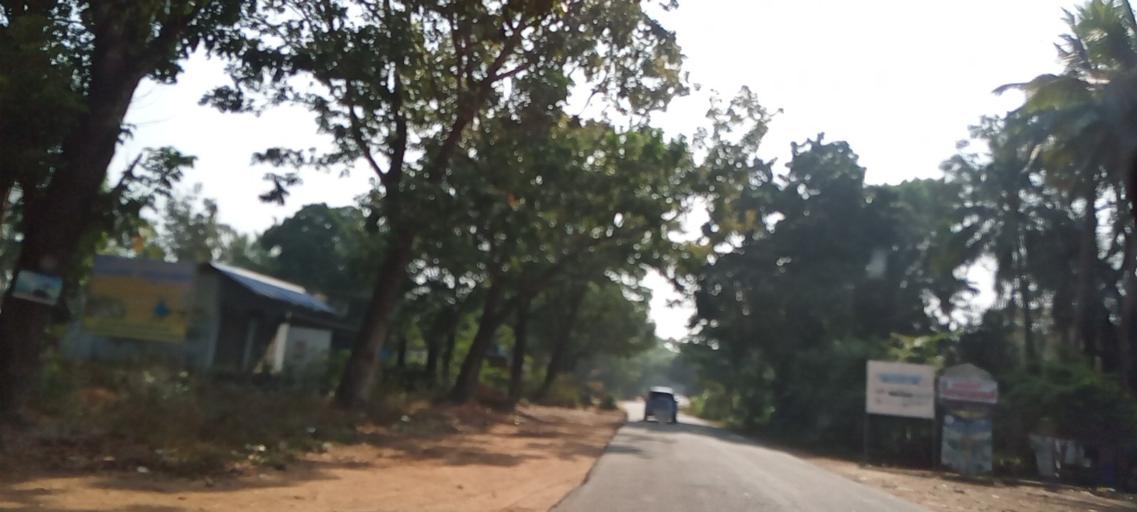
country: IN
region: Karnataka
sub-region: Udupi
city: Coondapoor
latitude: 13.5122
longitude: 74.7750
